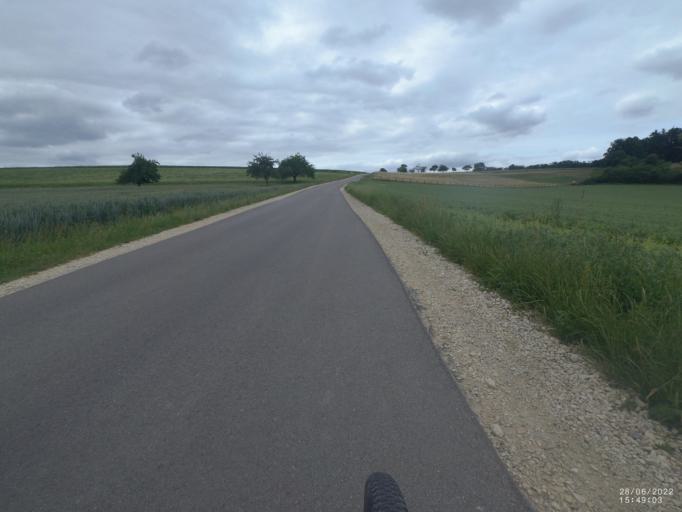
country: DE
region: Baden-Wuerttemberg
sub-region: Regierungsbezirk Stuttgart
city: Gerstetten
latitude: 48.6457
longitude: 10.0014
